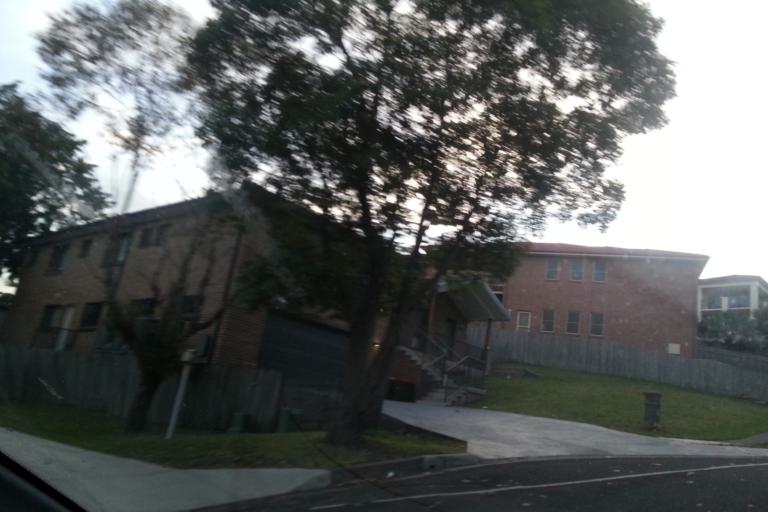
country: AU
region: New South Wales
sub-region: Wollongong
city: Keiraville
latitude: -34.4150
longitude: 150.8651
